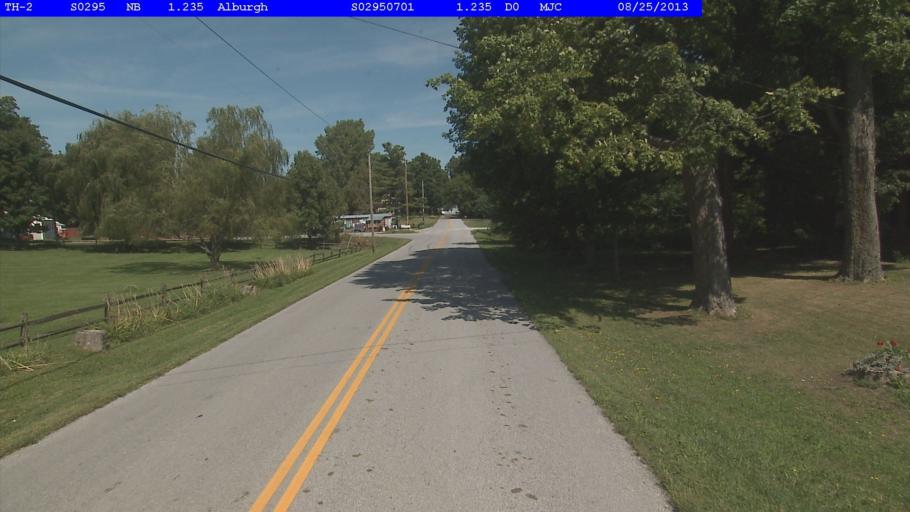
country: US
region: Vermont
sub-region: Franklin County
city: Swanton
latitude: 44.9912
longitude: -73.2233
